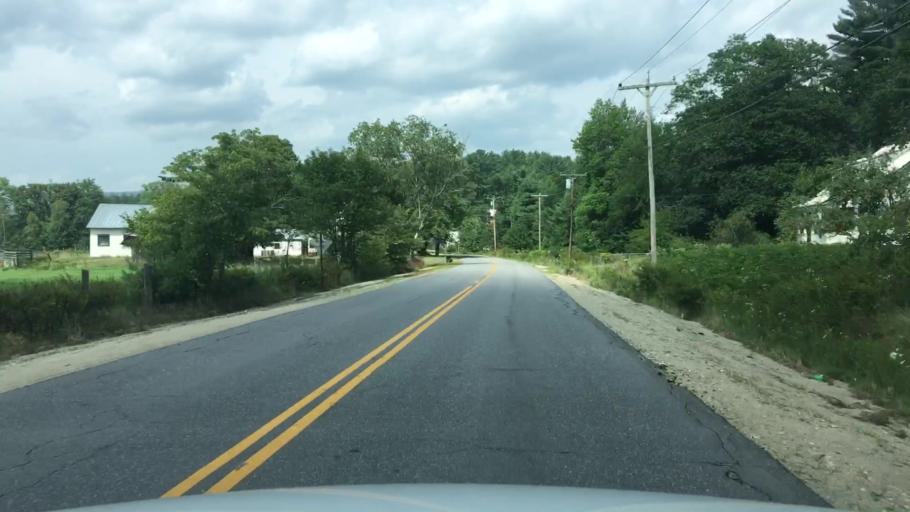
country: US
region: Maine
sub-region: Oxford County
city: Rumford
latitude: 44.5188
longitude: -70.6249
